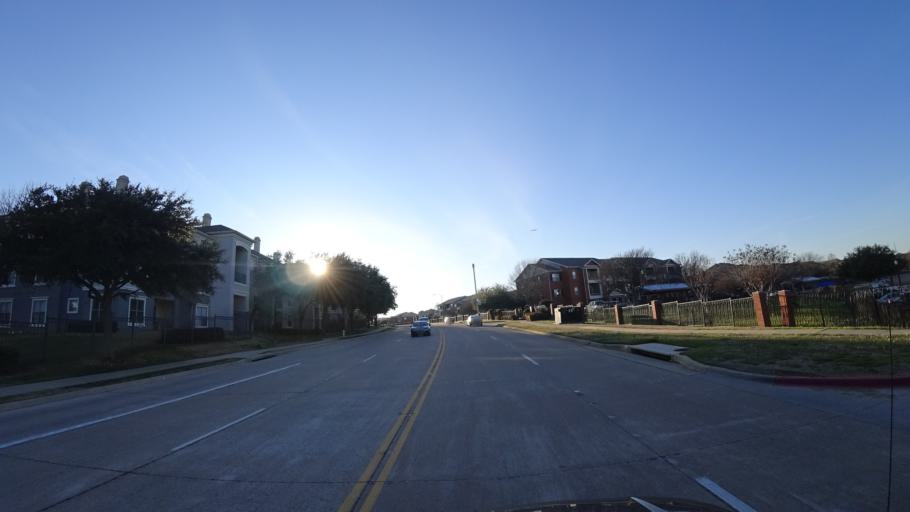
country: US
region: Texas
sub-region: Denton County
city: Lewisville
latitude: 32.9986
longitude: -96.9838
